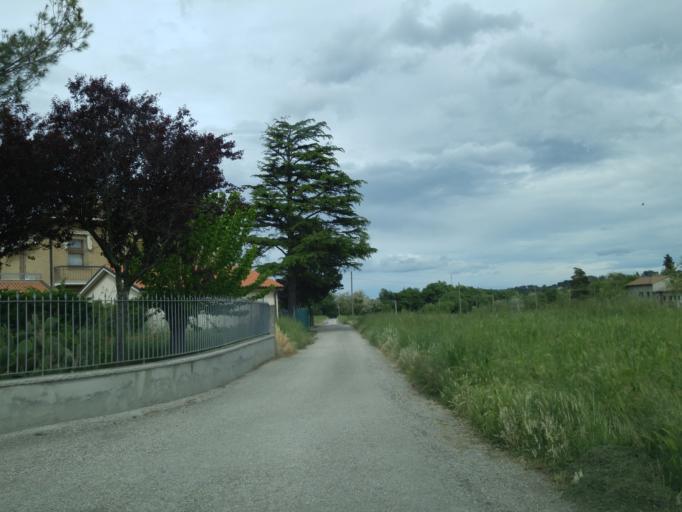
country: IT
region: The Marches
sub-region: Provincia di Pesaro e Urbino
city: Fossombrone
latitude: 43.6965
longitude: 12.8435
